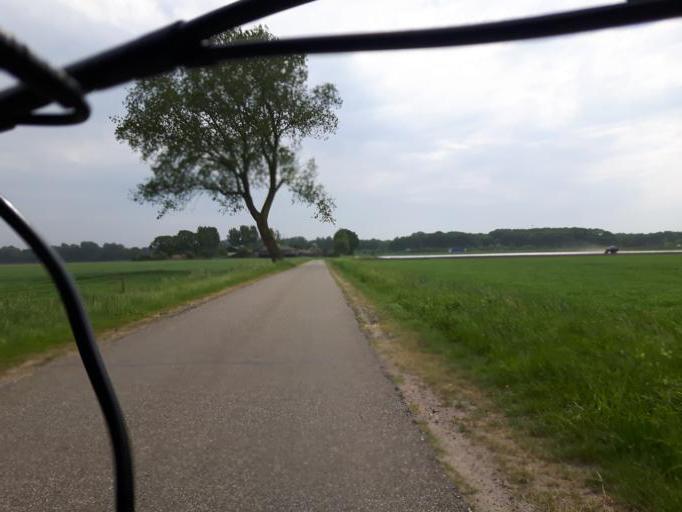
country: NL
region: North Brabant
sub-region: Gemeente Bergen op Zoom
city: Lepelstraat
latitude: 51.5356
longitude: 4.3082
